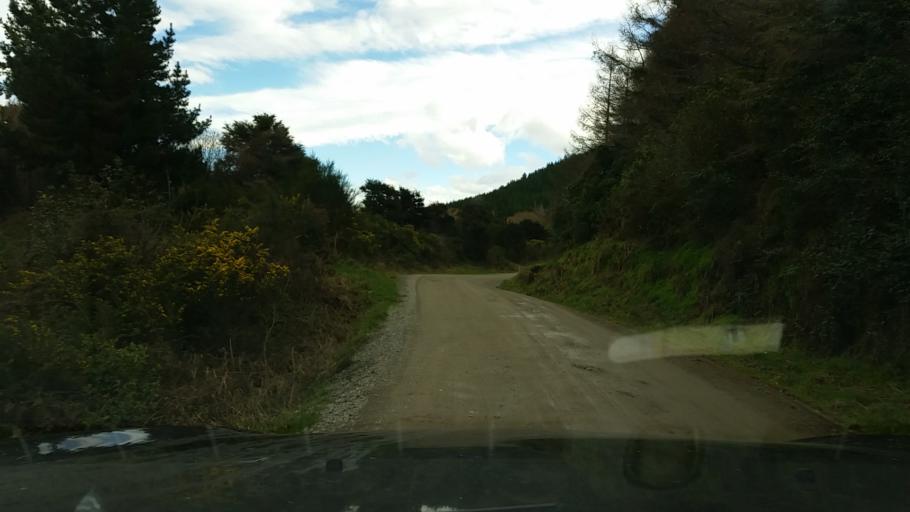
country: NZ
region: Nelson
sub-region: Nelson City
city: Nelson
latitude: -41.5770
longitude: 173.4377
